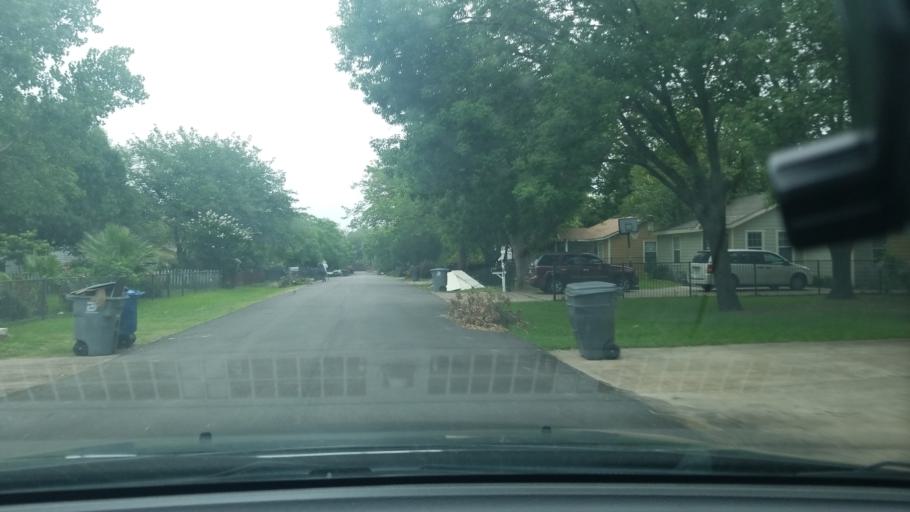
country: US
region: Texas
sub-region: Dallas County
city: Balch Springs
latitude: 32.7578
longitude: -96.6764
